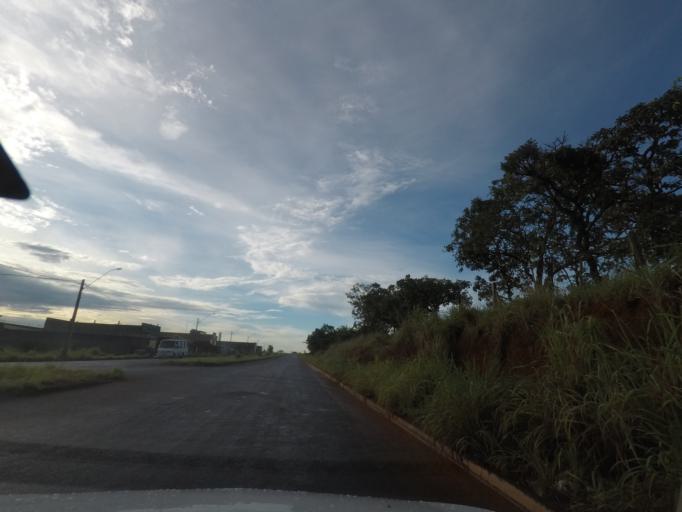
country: BR
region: Goias
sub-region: Trindade
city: Trindade
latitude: -16.7519
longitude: -49.3832
